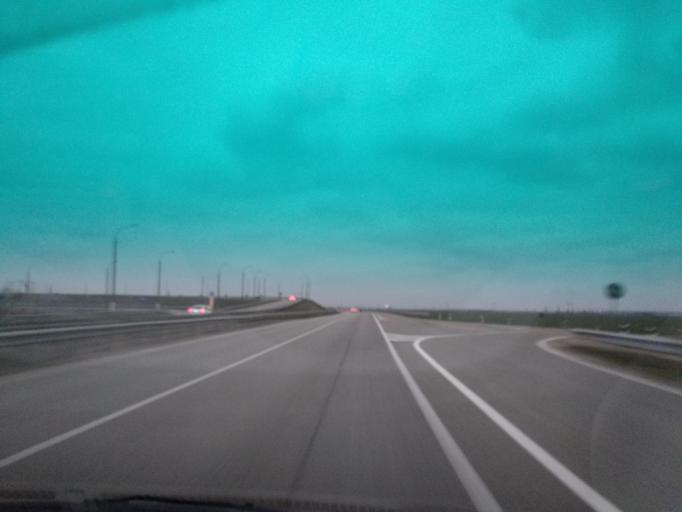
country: RU
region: Adygeya
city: Adygeysk
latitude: 44.8951
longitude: 39.1649
